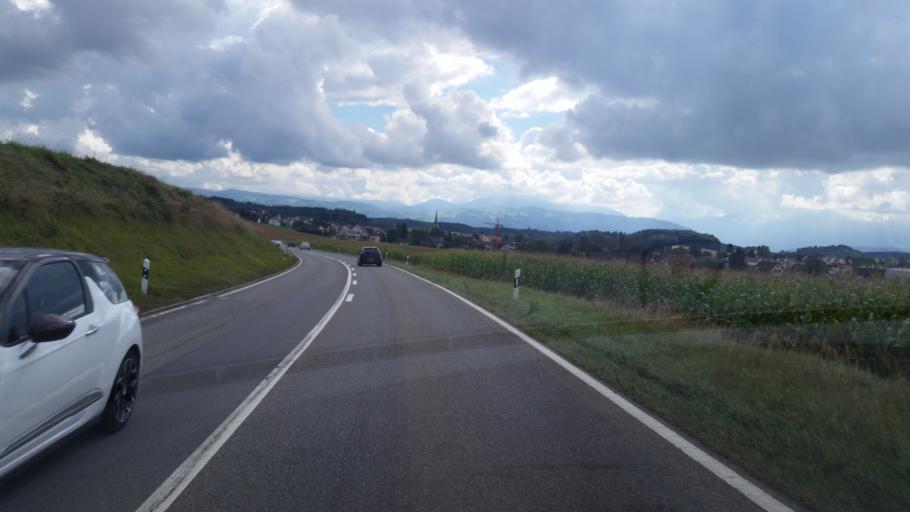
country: CH
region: Zurich
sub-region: Bezirk Affoltern
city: Mettmenstetten
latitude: 47.2526
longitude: 8.4539
